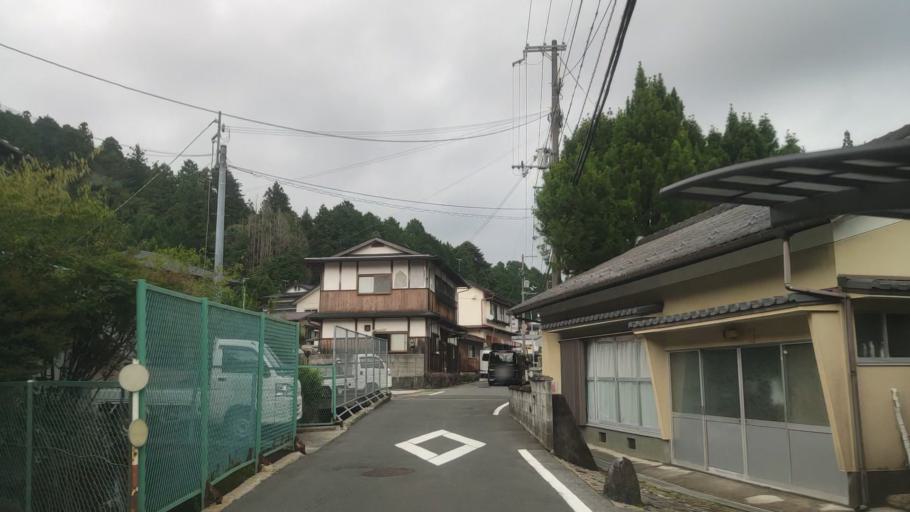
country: JP
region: Wakayama
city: Koya
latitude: 34.2162
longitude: 135.6071
